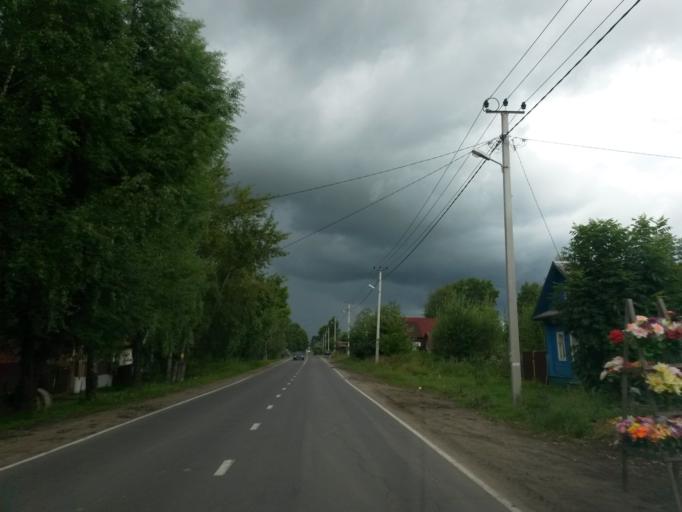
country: RU
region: Jaroslavl
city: Tutayev
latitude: 57.8798
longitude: 39.5567
